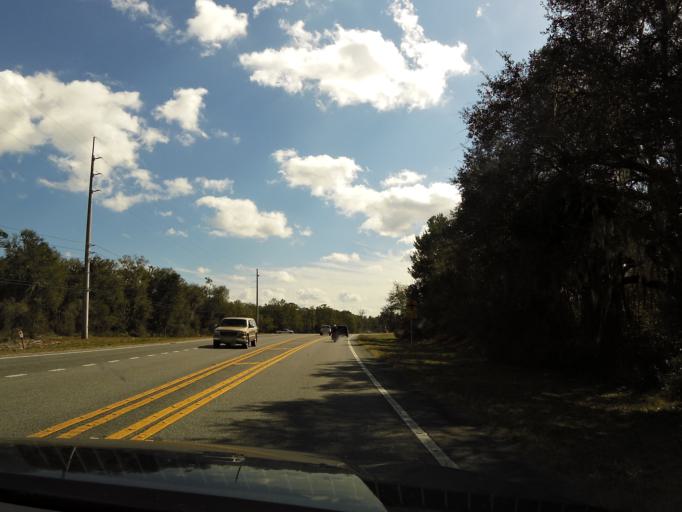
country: US
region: Florida
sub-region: Volusia County
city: De Leon Springs
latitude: 29.1365
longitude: -81.3537
